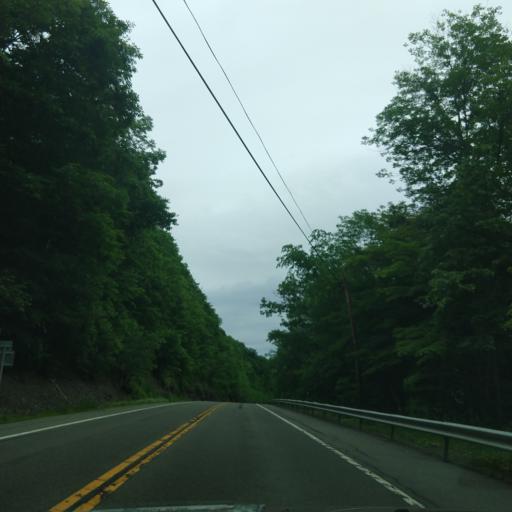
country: US
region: New York
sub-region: Cortland County
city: McGraw
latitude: 42.4905
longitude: -76.0720
